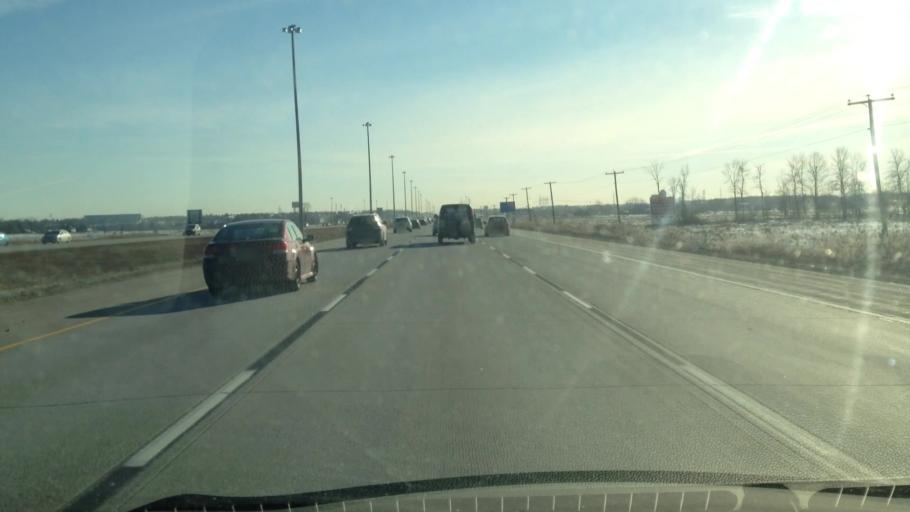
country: CA
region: Quebec
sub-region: Laurentides
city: Blainville
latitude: 45.7008
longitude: -73.9501
